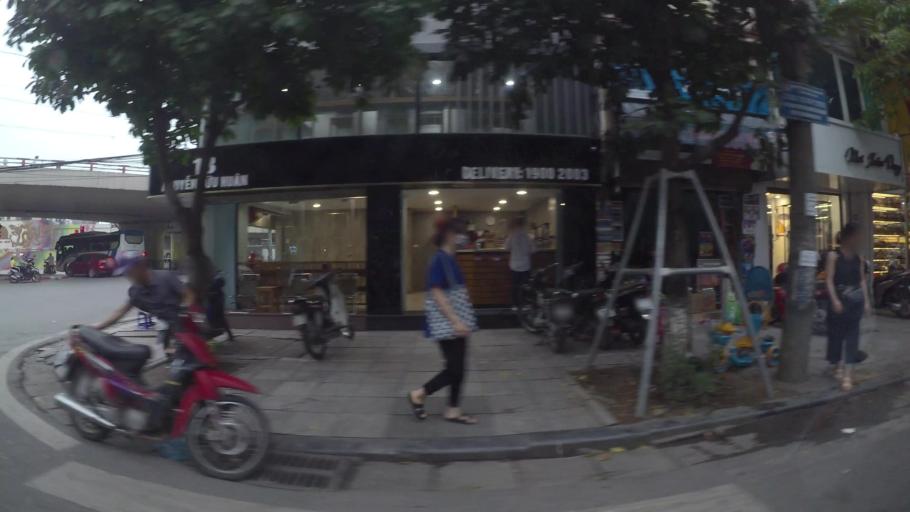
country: VN
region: Ha Noi
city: Hoan Kiem
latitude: 21.0348
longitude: 105.8544
